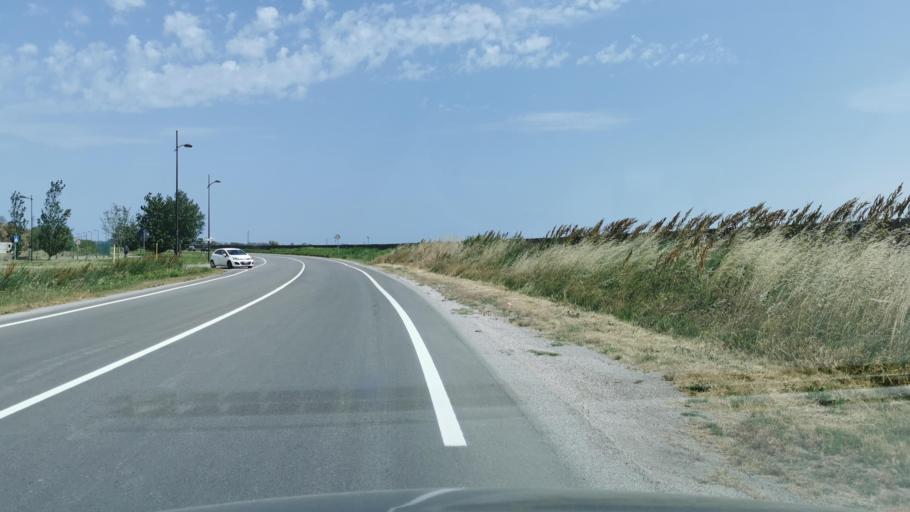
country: IT
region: Emilia-Romagna
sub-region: Provincia di Ferrara
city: Comacchio
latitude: 44.6784
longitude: 12.2033
